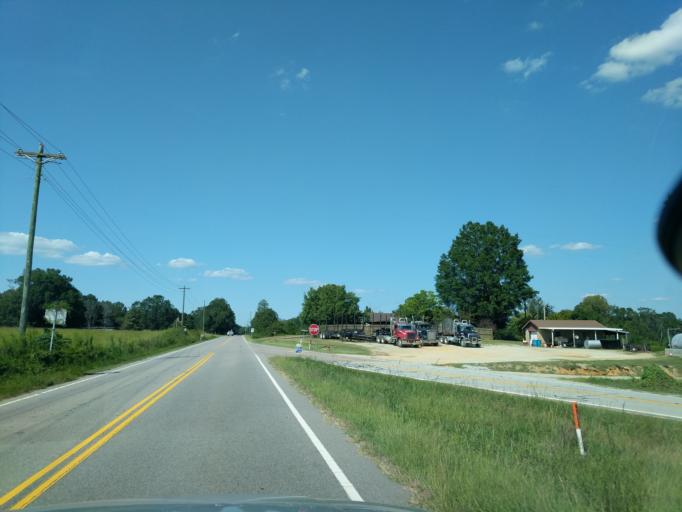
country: US
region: South Carolina
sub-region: Newberry County
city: Prosperity
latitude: 34.1306
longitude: -81.5416
